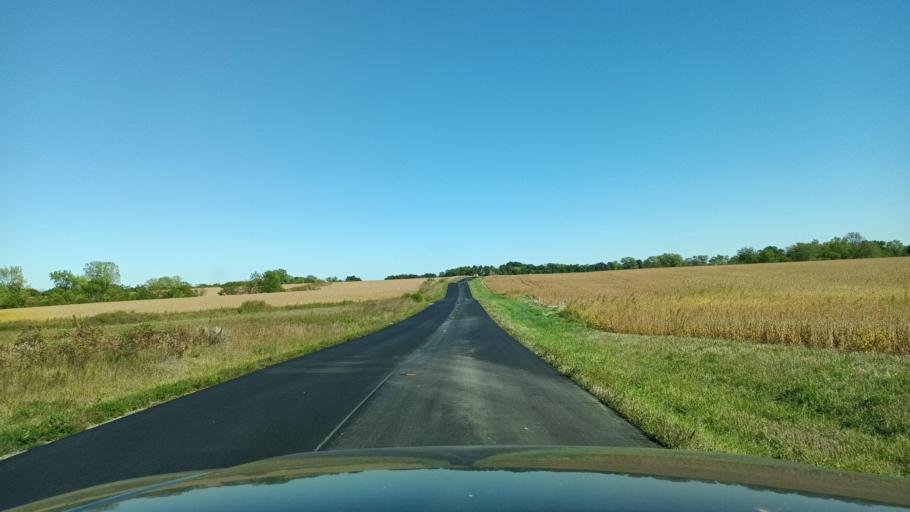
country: US
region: Missouri
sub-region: Macon County
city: La Plata
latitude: 39.9274
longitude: -92.5467
